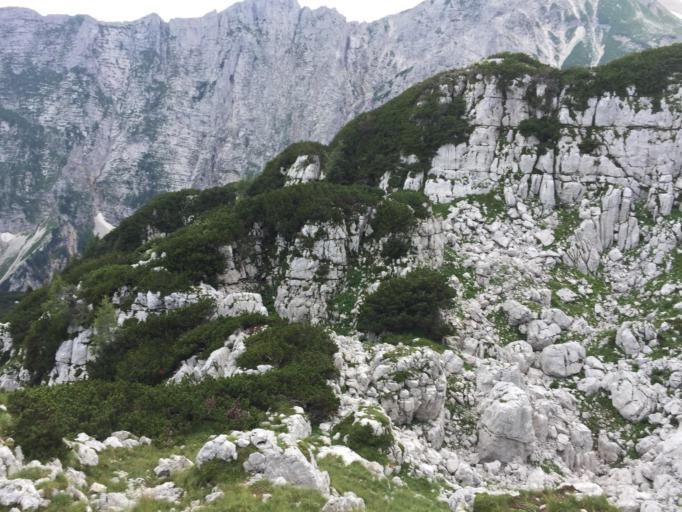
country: SI
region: Bovec
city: Bovec
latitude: 46.3884
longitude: 13.5406
